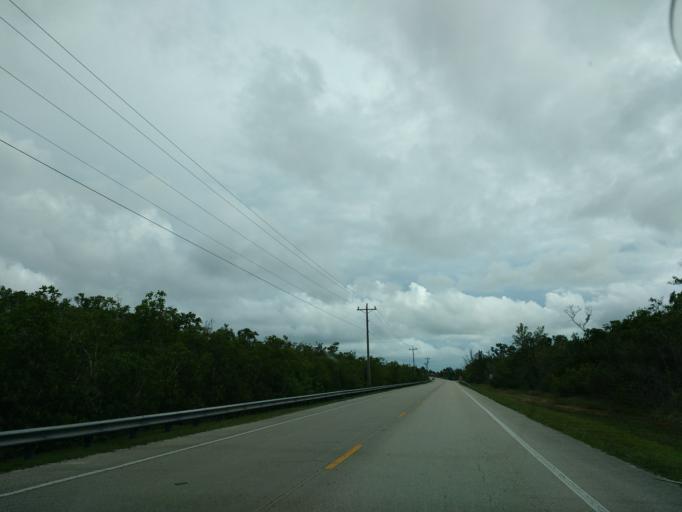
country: US
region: Florida
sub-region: Collier County
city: Marco
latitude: 25.8763
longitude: -81.3813
